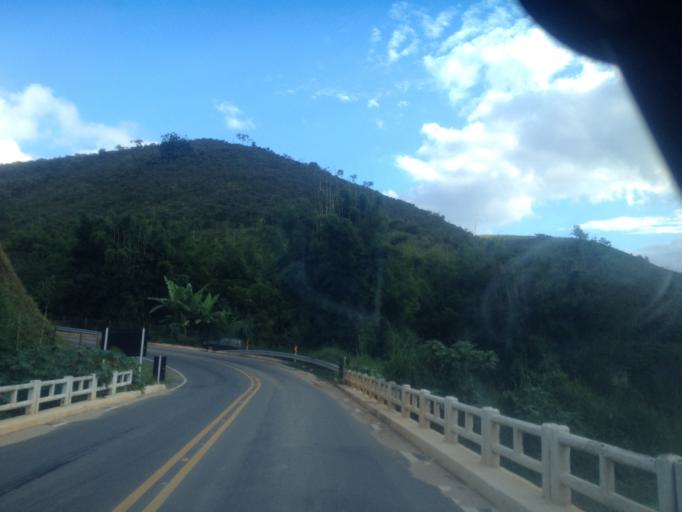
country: BR
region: Rio de Janeiro
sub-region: Quatis
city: Quatis
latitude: -22.2832
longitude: -44.2588
